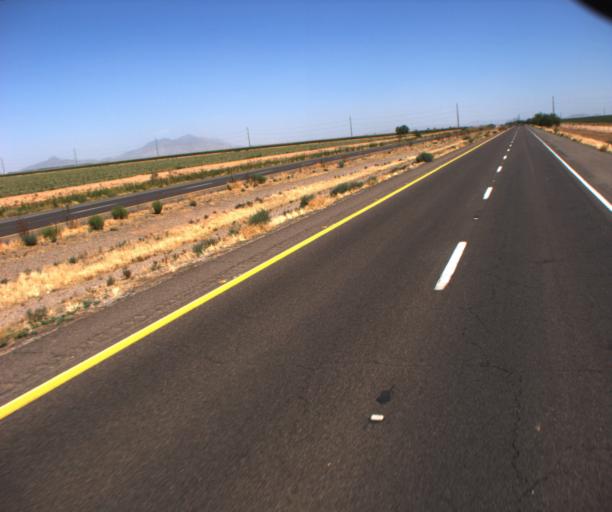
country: US
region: Arizona
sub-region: Pinal County
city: Maricopa
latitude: 32.9517
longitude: -112.0479
